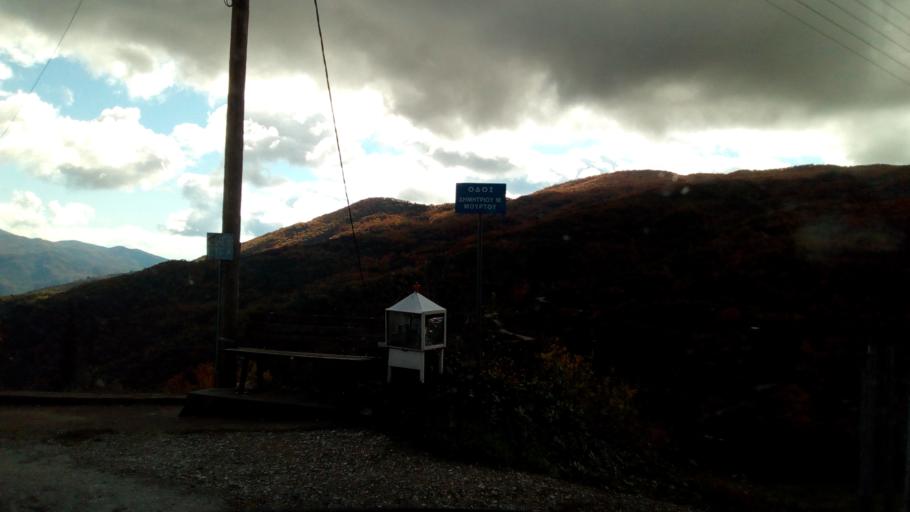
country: GR
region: West Greece
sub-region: Nomos Aitolias kai Akarnanias
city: Nafpaktos
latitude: 38.5634
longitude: 21.9728
